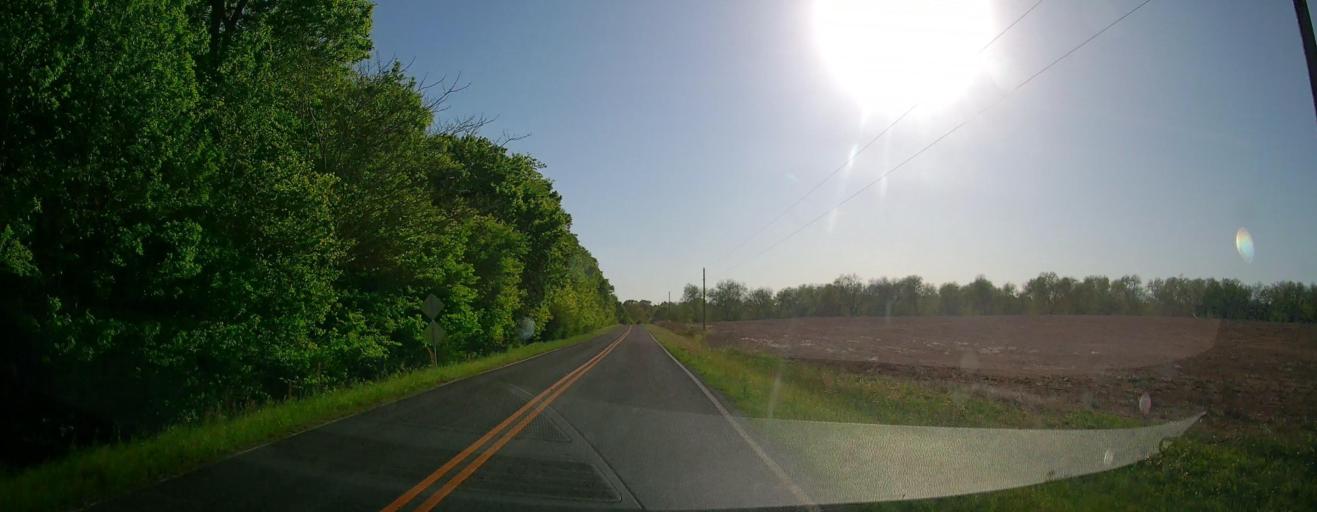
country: US
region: Georgia
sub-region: Macon County
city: Marshallville
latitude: 32.3840
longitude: -83.8618
